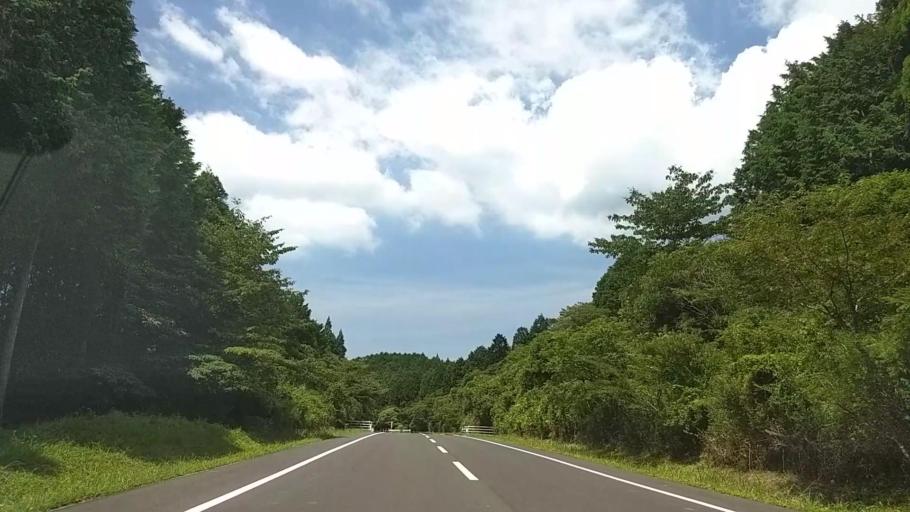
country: JP
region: Shizuoka
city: Fuji
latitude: 35.2521
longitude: 138.6956
